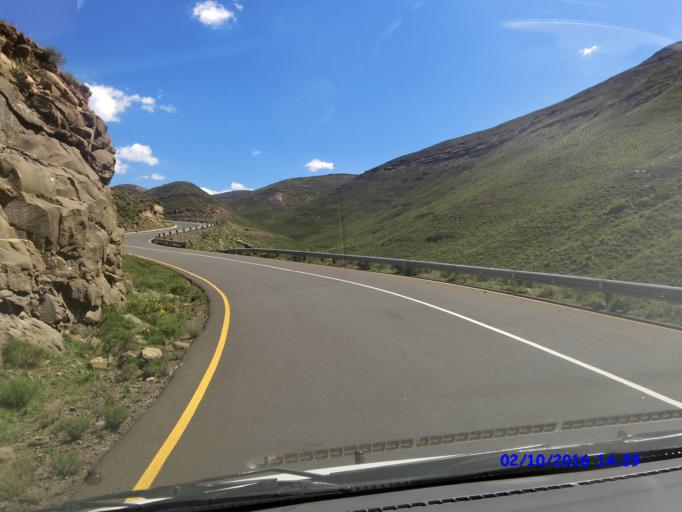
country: LS
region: Maseru
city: Nako
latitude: -29.5156
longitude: 28.0616
